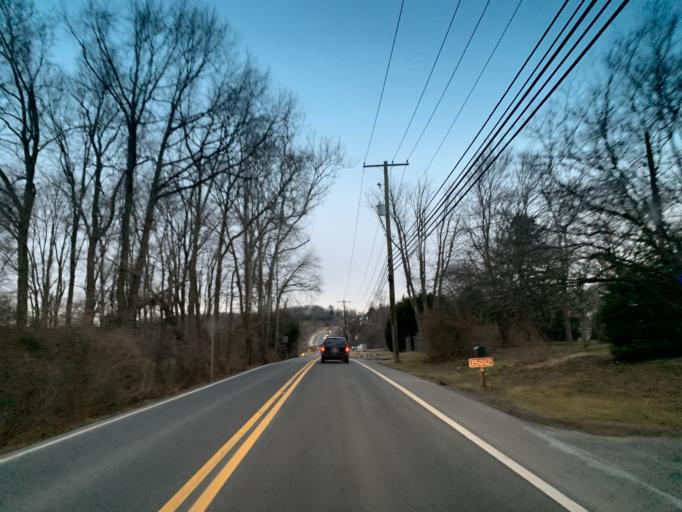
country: US
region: Maryland
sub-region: Montgomery County
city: Layhill
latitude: 39.1044
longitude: -77.0391
